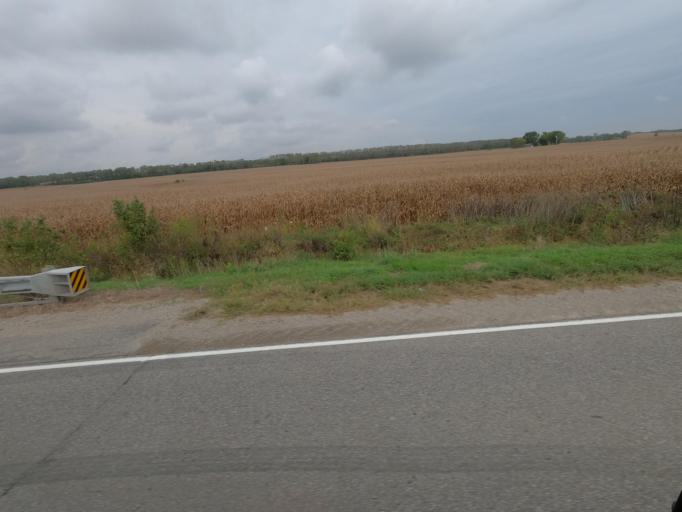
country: US
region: Iowa
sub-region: Wapello County
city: Ottumwa
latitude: 40.9089
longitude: -92.2085
